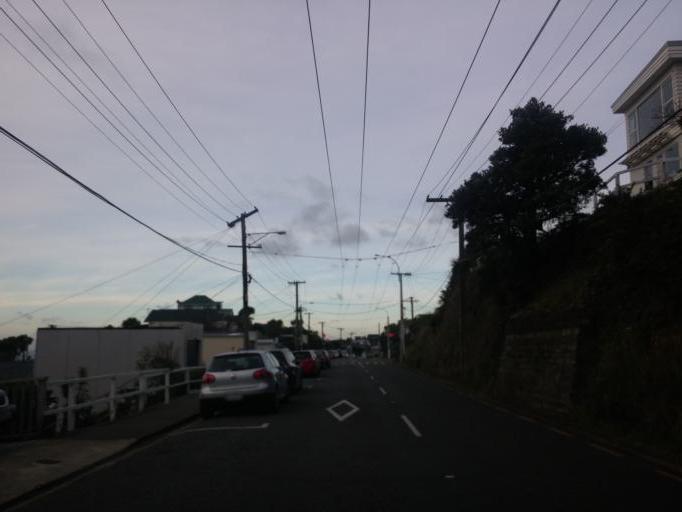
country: NZ
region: Wellington
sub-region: Wellington City
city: Brooklyn
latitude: -41.3148
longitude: 174.7655
